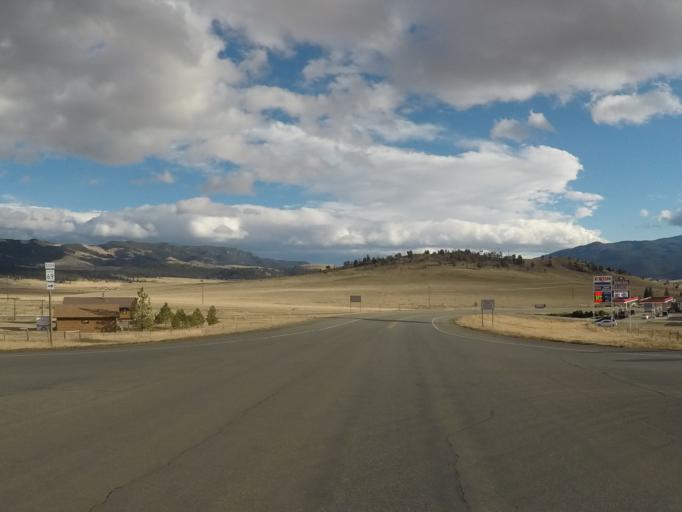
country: US
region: Montana
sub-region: Jefferson County
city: Boulder
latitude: 46.2458
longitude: -112.1179
